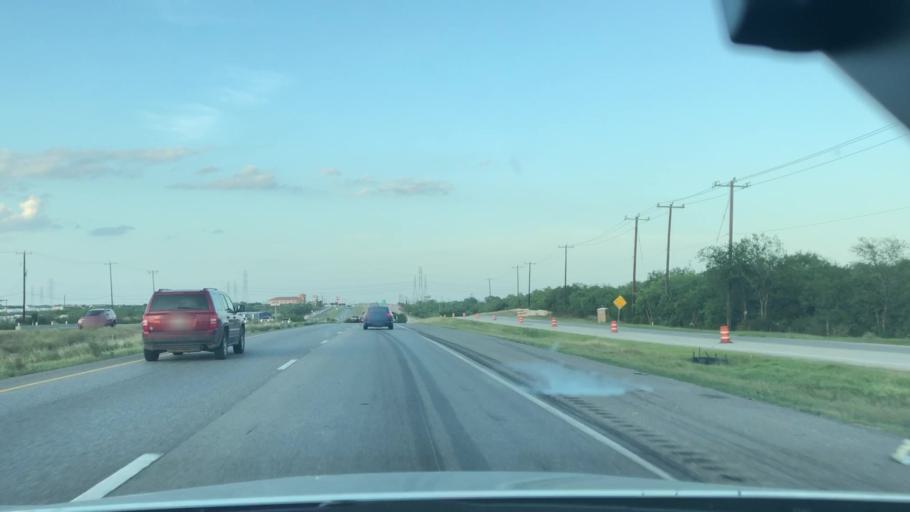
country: US
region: Texas
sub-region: Bexar County
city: Kirby
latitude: 29.4557
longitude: -98.3338
